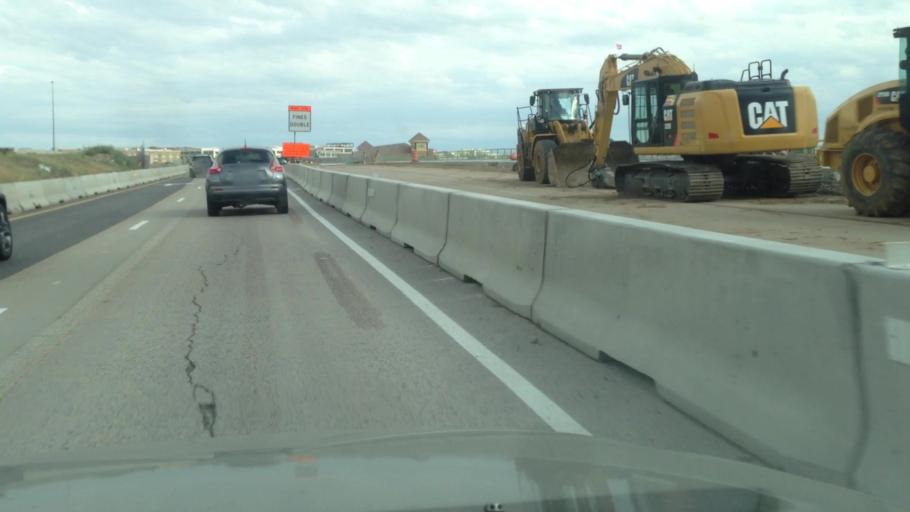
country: US
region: Colorado
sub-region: Adams County
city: Lone Tree
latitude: 39.5593
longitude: -104.8823
